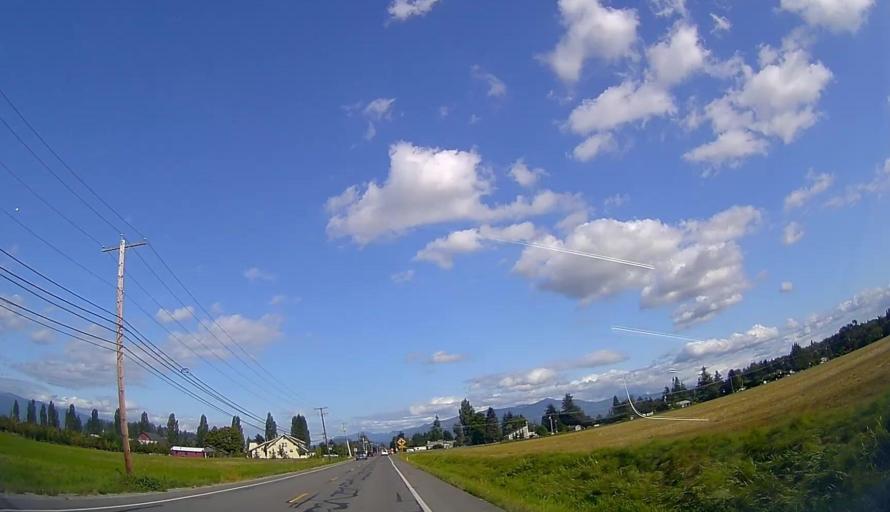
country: US
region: Washington
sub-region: Skagit County
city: Burlington
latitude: 48.4720
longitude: -122.3601
